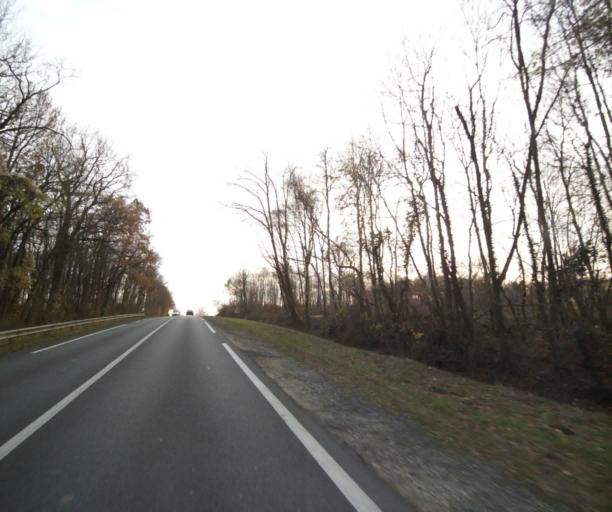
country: FR
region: Poitou-Charentes
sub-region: Departement de la Charente-Maritime
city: Fontcouverte
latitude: 45.7935
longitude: -0.5678
